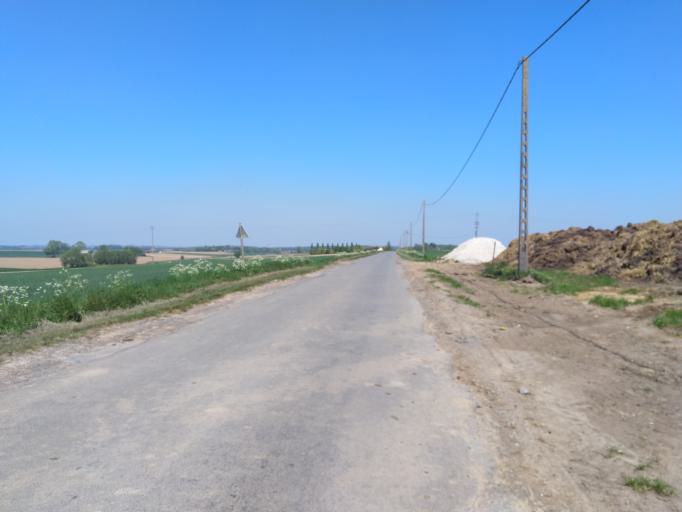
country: BE
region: Wallonia
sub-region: Province du Hainaut
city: Enghien
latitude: 50.6500
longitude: 4.0303
